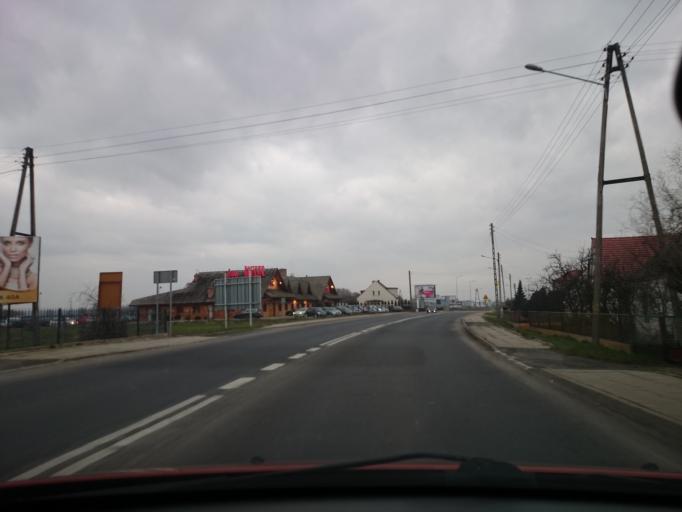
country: PL
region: Opole Voivodeship
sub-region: Powiat opolski
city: Chroscina
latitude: 50.6861
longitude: 17.8139
